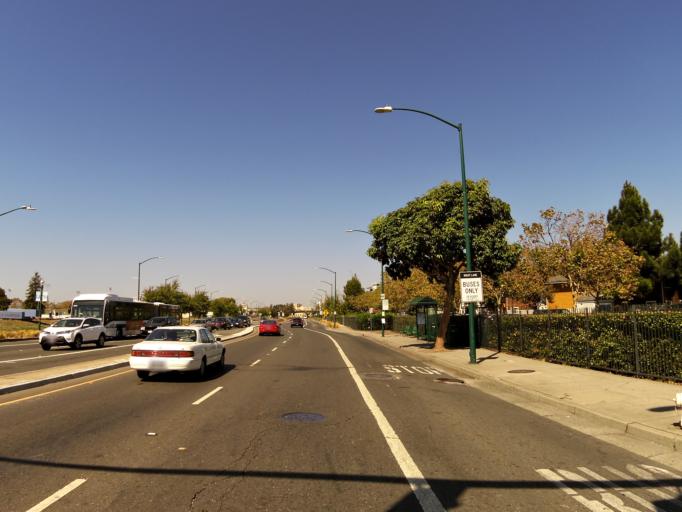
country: US
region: California
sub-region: Alameda County
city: Oakland
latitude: 37.7799
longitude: -122.2764
